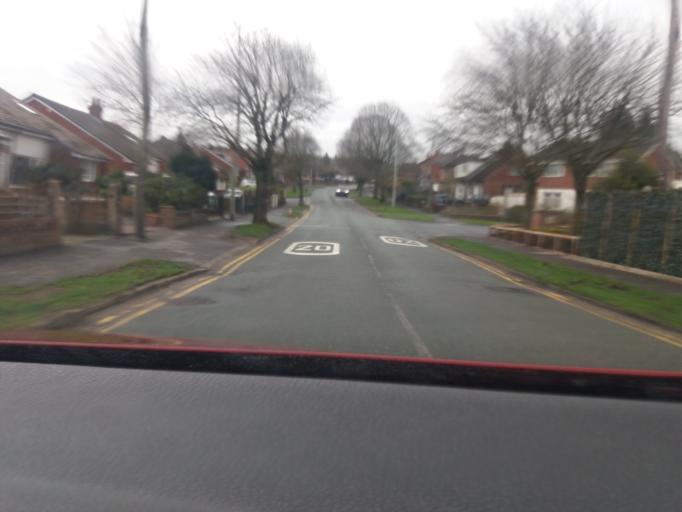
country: GB
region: England
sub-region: Lancashire
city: Chorley
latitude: 53.6481
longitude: -2.6433
